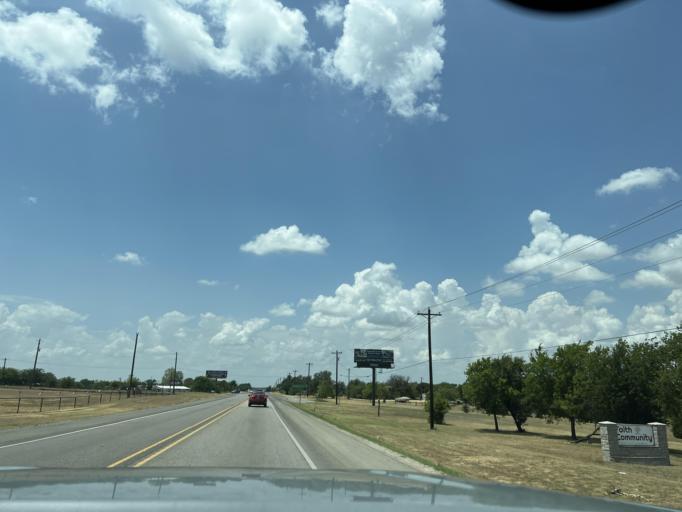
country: US
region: Texas
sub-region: Parker County
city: Weatherford
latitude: 32.8267
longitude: -97.7703
